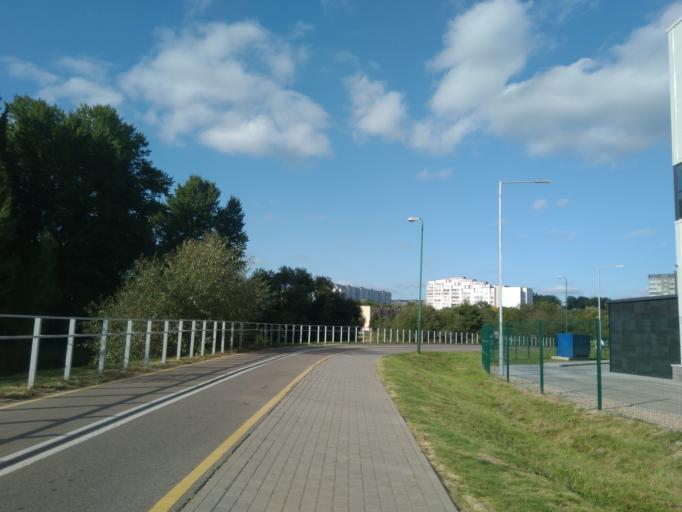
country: BY
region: Minsk
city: Minsk
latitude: 53.8677
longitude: 27.5896
